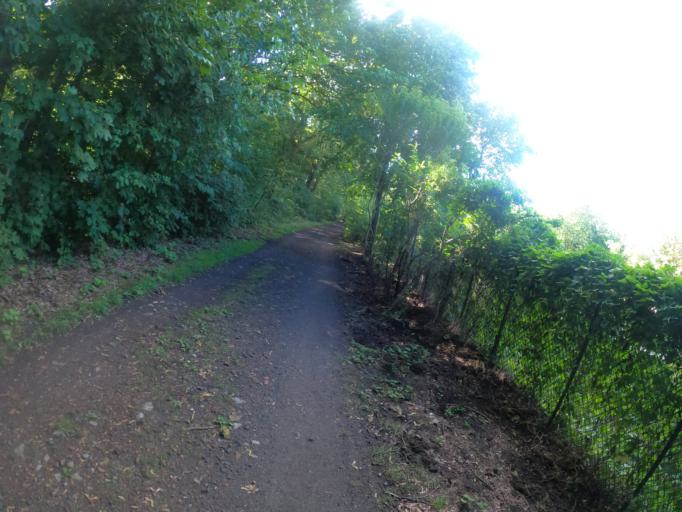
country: DE
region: Berlin
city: Siemensstadt
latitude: 52.5472
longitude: 13.2807
